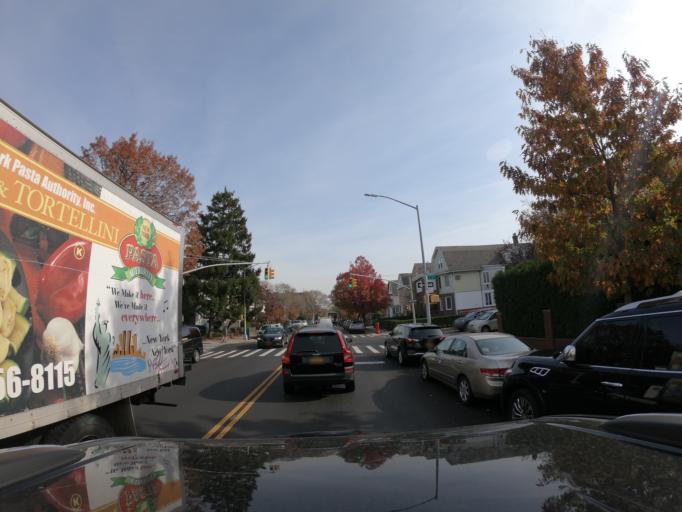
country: US
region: New York
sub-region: Kings County
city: Bensonhurst
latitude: 40.6116
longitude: -73.9717
